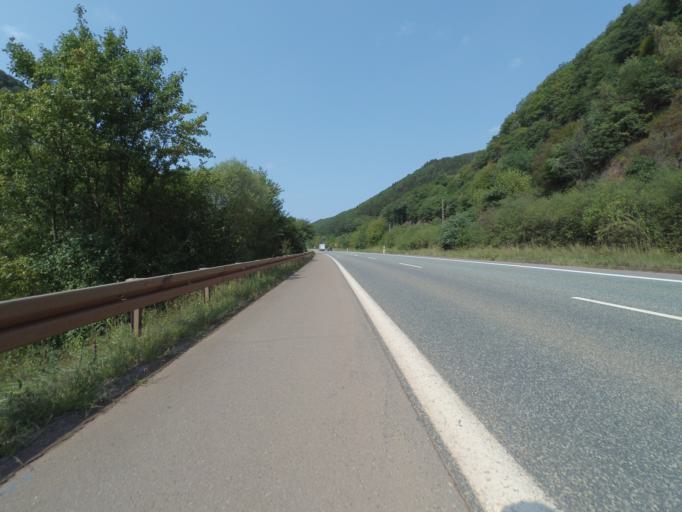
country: DE
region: Saarland
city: Saarhoelzbach
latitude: 49.5251
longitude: 6.6100
